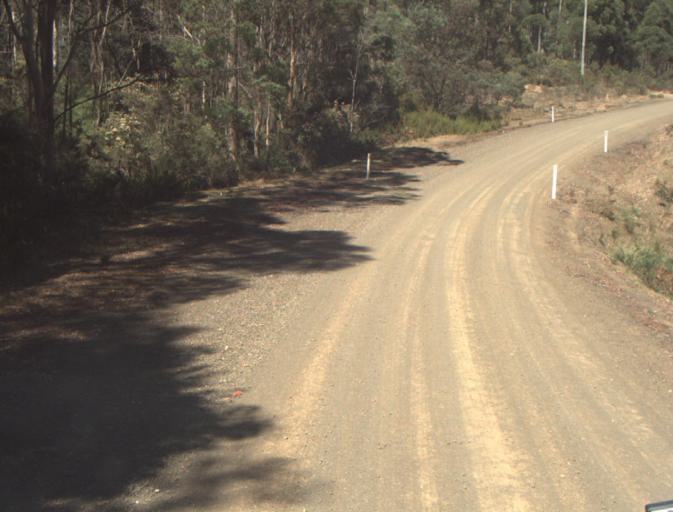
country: AU
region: Tasmania
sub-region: Launceston
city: Newstead
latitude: -41.3001
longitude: 147.3349
